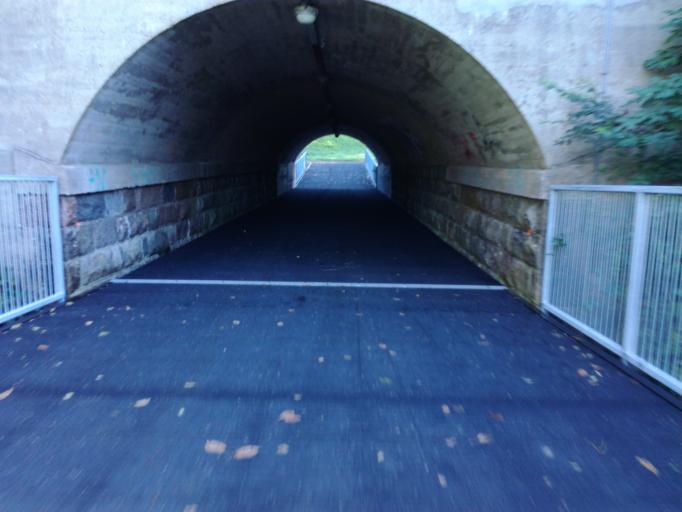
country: DK
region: South Denmark
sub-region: Vejle Kommune
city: Borkop
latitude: 55.6471
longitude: 9.6469
